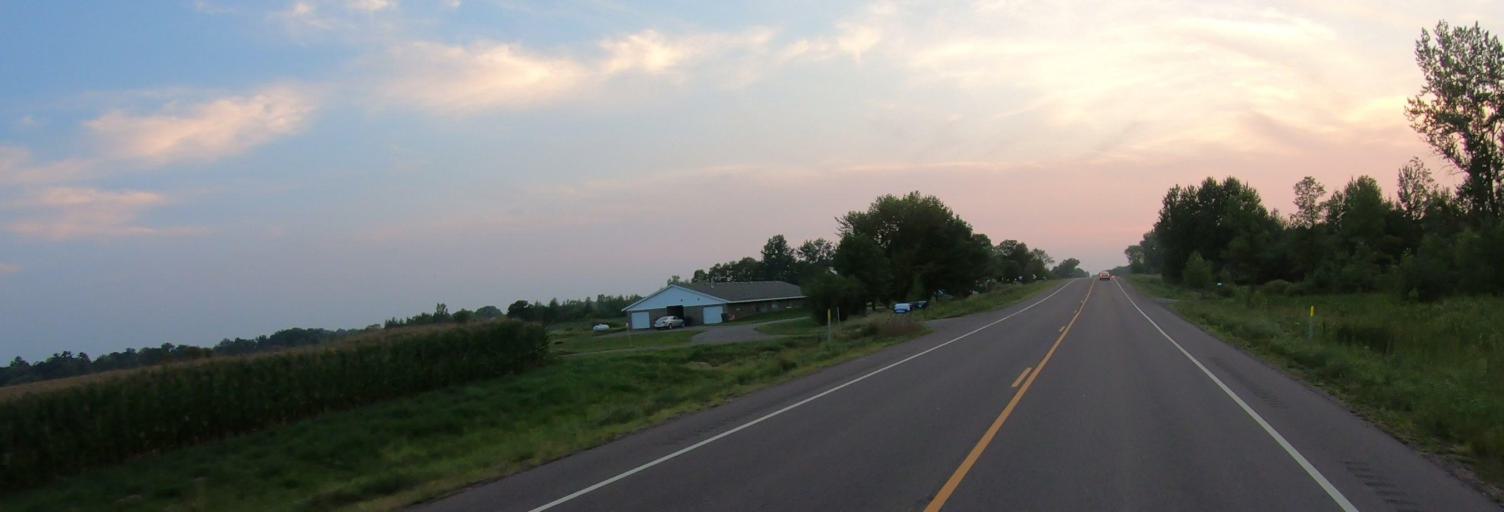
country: US
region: Minnesota
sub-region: Pine County
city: Rock Creek
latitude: 45.7736
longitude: -92.9470
